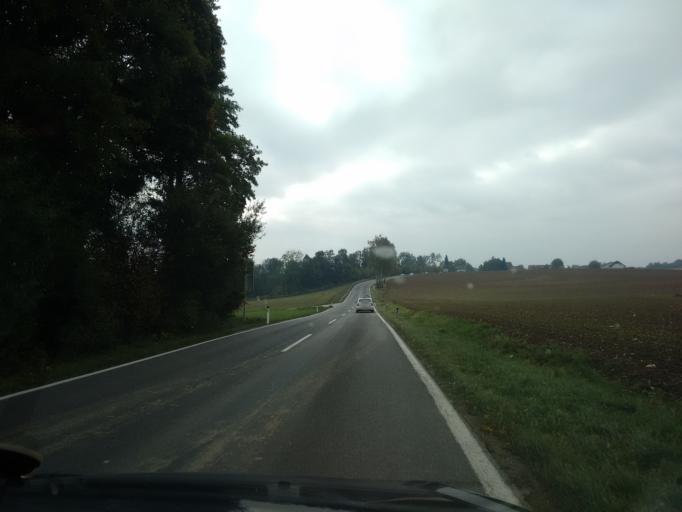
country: AT
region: Upper Austria
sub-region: Politischer Bezirk Steyr-Land
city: Bad Hall
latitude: 48.0609
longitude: 14.1971
